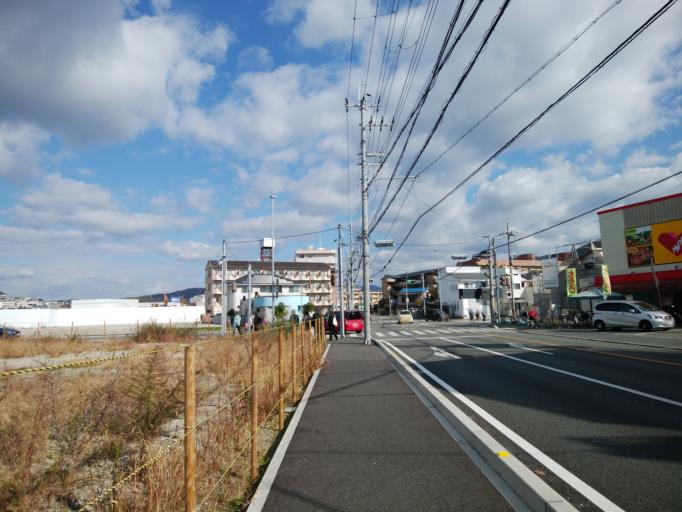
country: JP
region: Osaka
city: Ikeda
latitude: 34.8345
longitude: 135.4197
